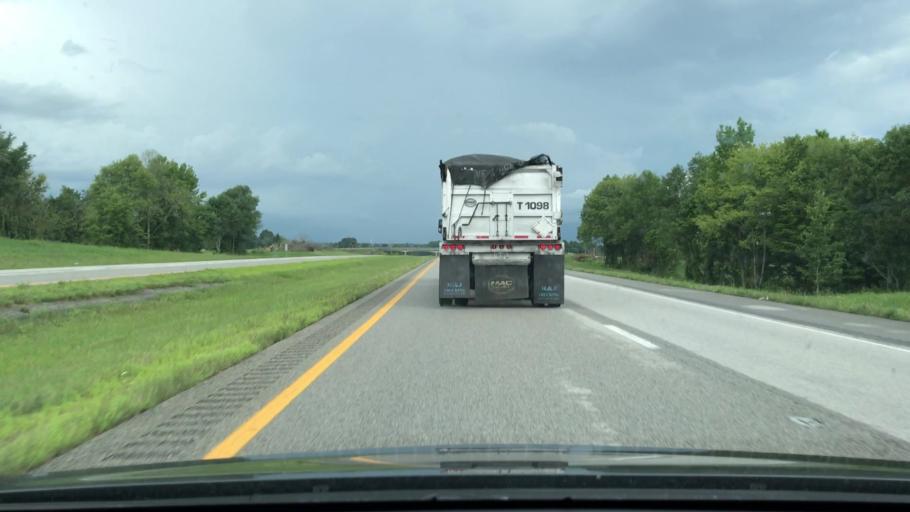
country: US
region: Kentucky
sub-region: Russell County
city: Russell Springs
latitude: 37.0864
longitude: -84.9251
